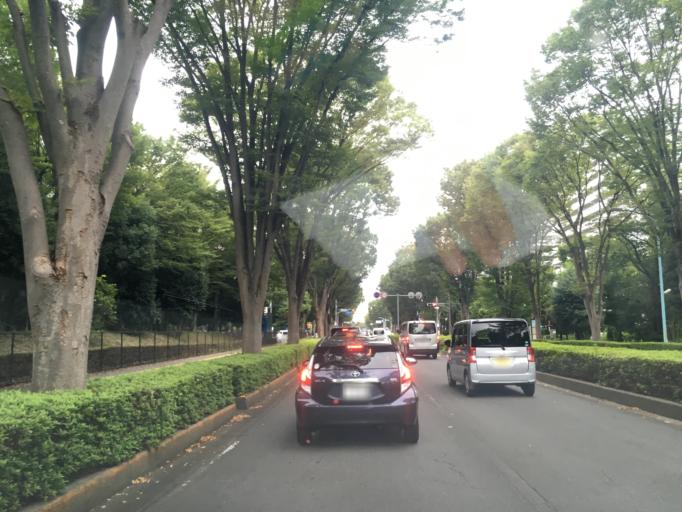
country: JP
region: Saitama
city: Tokorozawa
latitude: 35.8009
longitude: 139.4653
